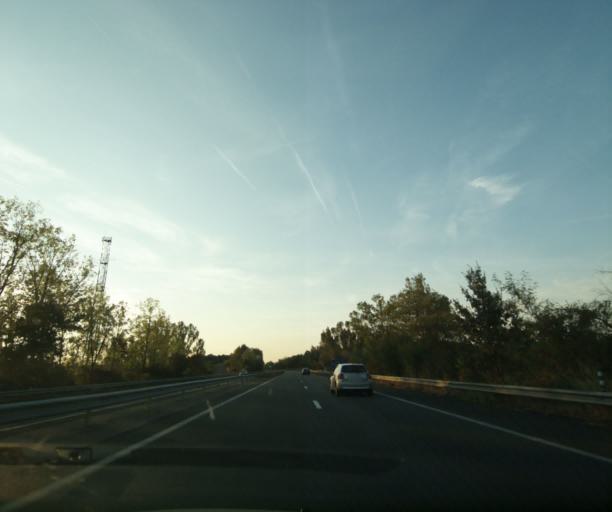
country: FR
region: Aquitaine
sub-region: Departement du Lot-et-Garonne
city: Buzet-sur-Baise
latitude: 44.2351
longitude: 0.3260
